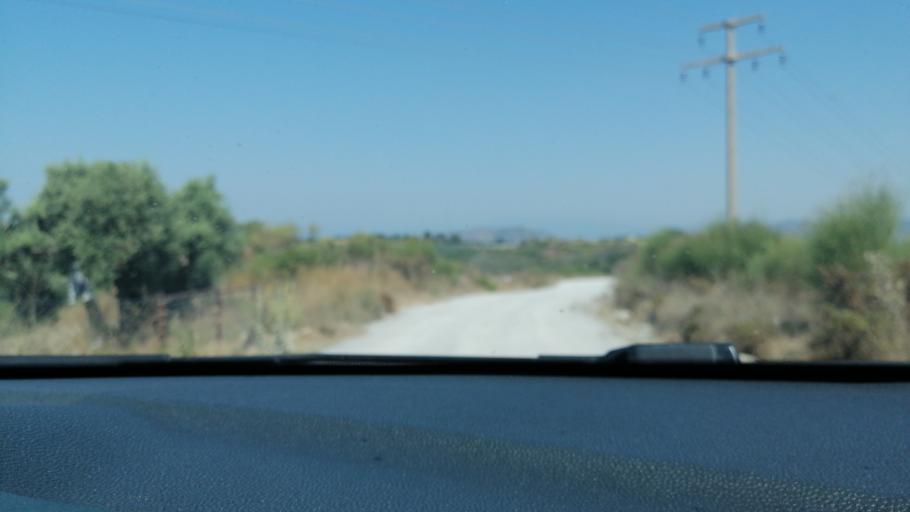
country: TR
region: Aydin
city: Davutlar
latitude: 37.7777
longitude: 27.3145
